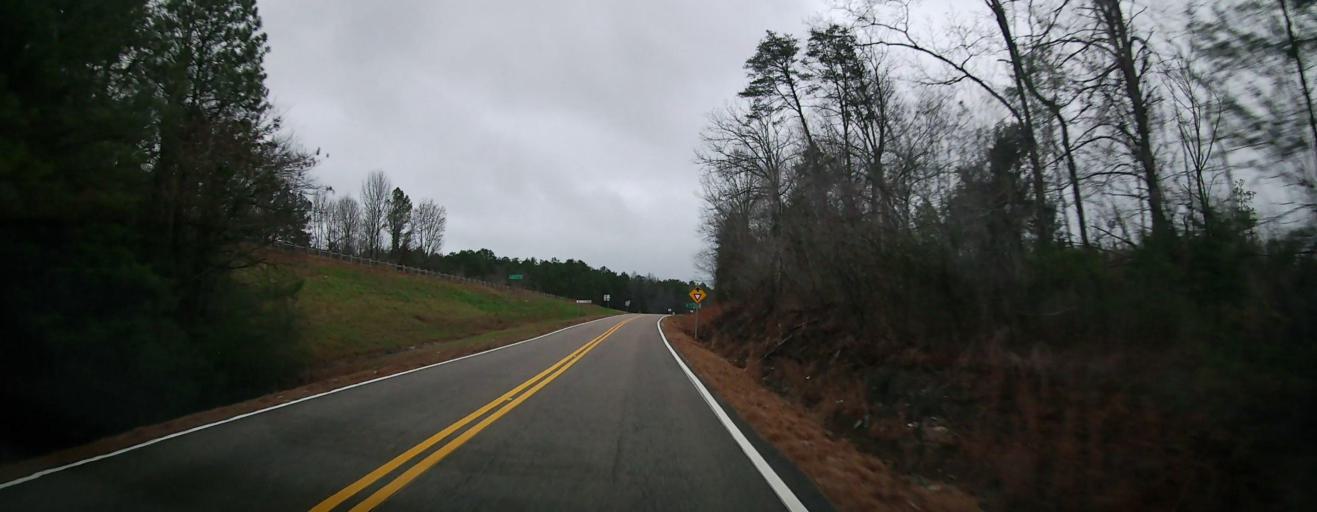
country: US
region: Alabama
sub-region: Bibb County
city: Centreville
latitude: 33.0274
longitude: -87.1434
